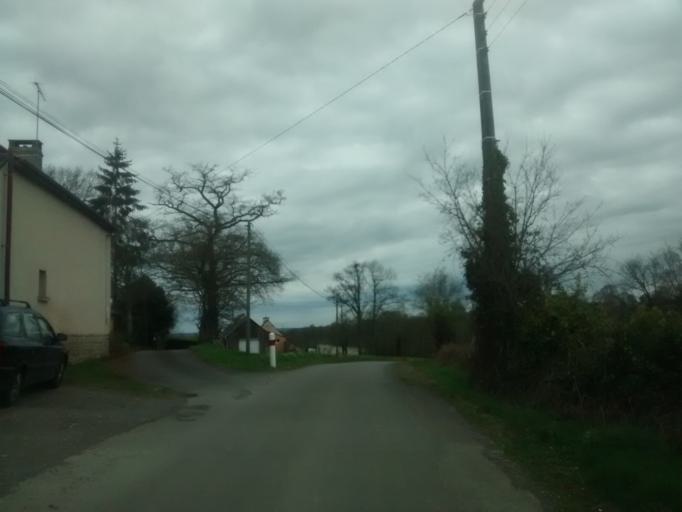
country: FR
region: Brittany
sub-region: Departement d'Ille-et-Vilaine
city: Erce-pres-Liffre
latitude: 48.2407
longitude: -1.5201
